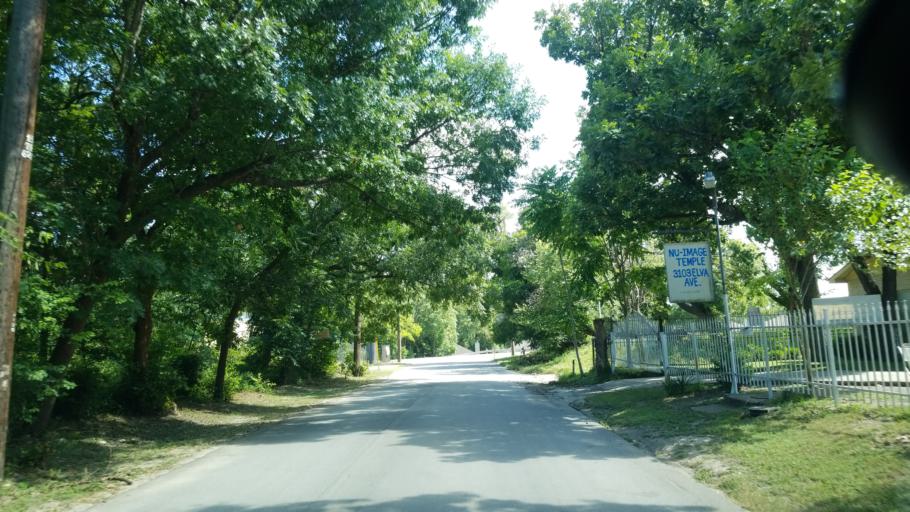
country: US
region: Texas
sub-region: Dallas County
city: Balch Springs
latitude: 32.7643
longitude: -96.6971
